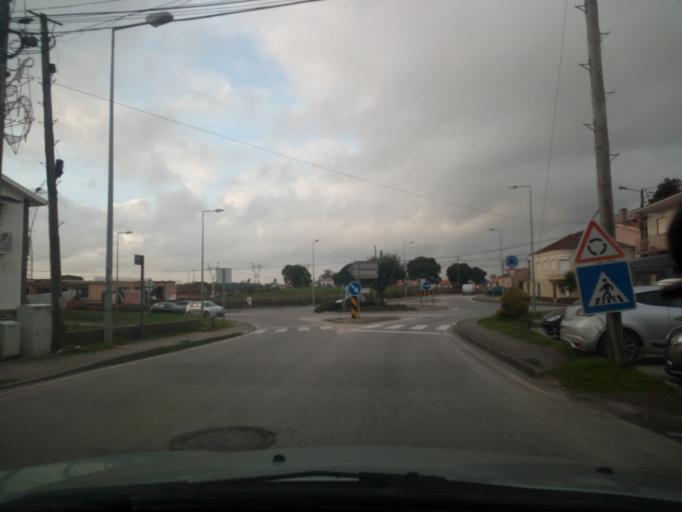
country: PT
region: Aveiro
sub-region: Agueda
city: Agueda
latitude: 40.5588
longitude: -8.4672
